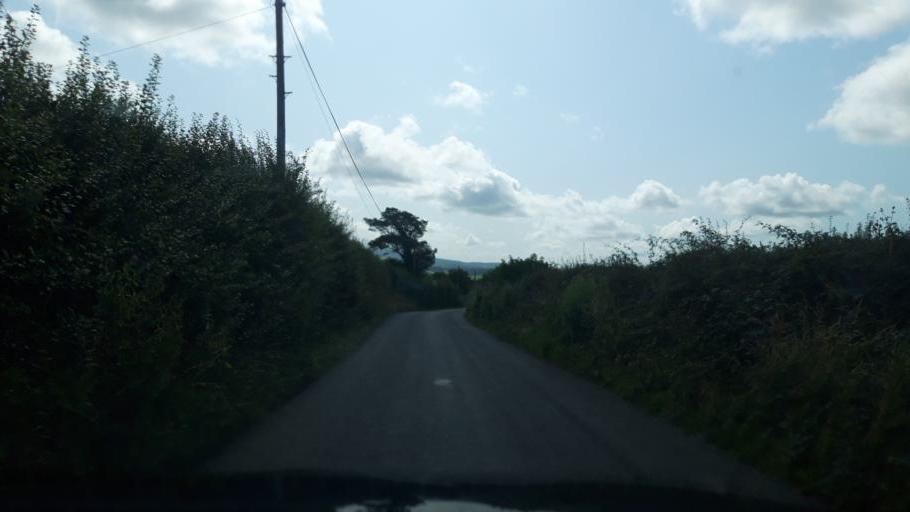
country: IE
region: Leinster
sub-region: Kilkenny
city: Graiguenamanagh
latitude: 52.5496
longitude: -6.9706
